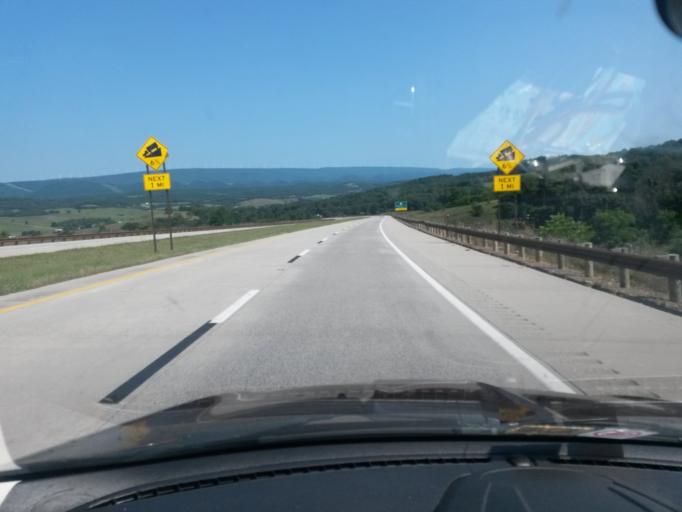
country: US
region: West Virginia
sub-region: Hardy County
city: Moorefield
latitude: 39.1336
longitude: -79.0583
